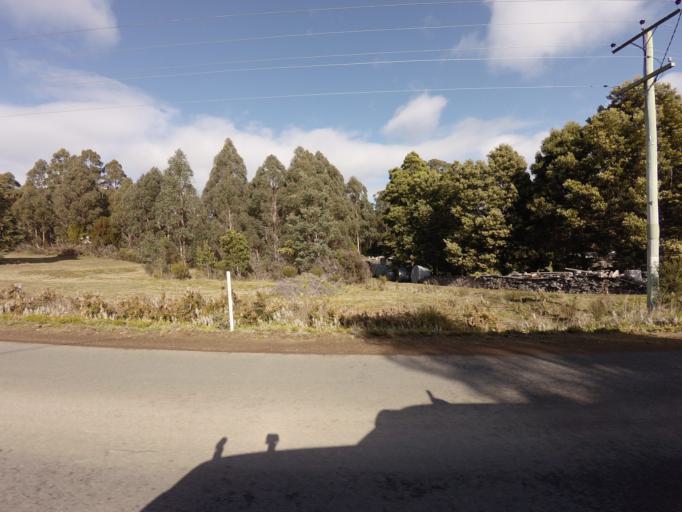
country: AU
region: Tasmania
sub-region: Huon Valley
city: Geeveston
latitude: -43.3375
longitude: 146.9712
